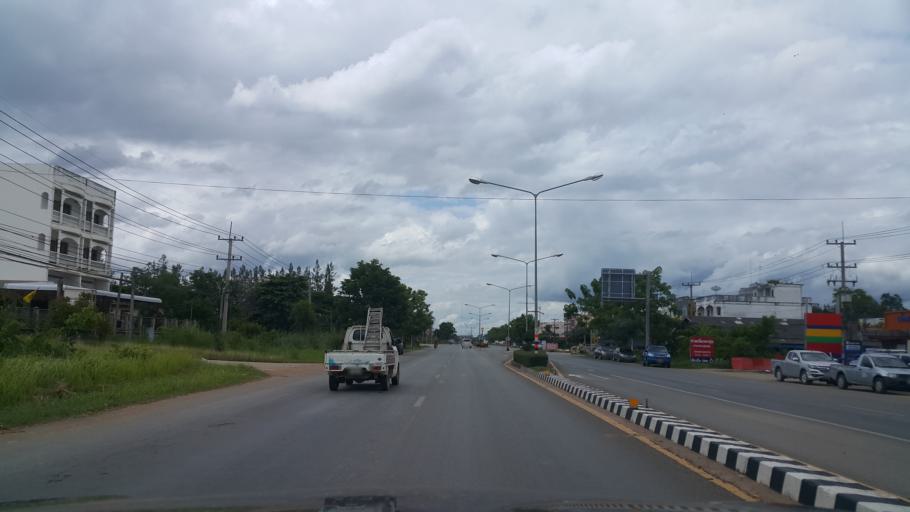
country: TH
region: Sukhothai
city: Sukhothai
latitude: 17.0115
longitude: 99.8067
